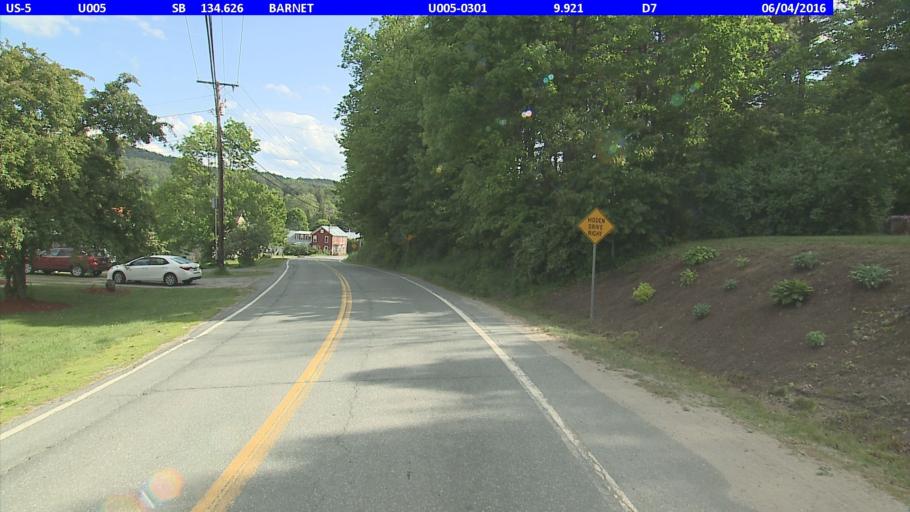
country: US
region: Vermont
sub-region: Caledonia County
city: Saint Johnsbury
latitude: 44.3790
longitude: -72.0270
